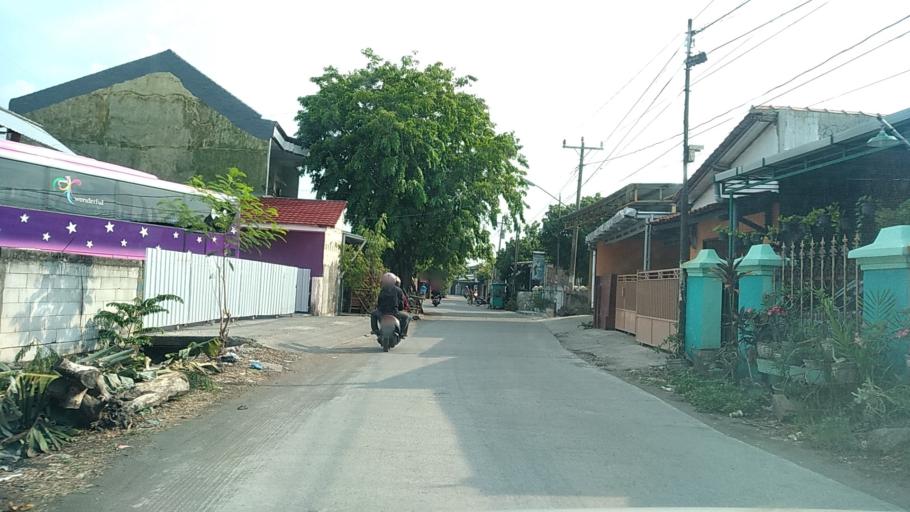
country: ID
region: Central Java
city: Semarang
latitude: -6.9954
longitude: 110.4658
